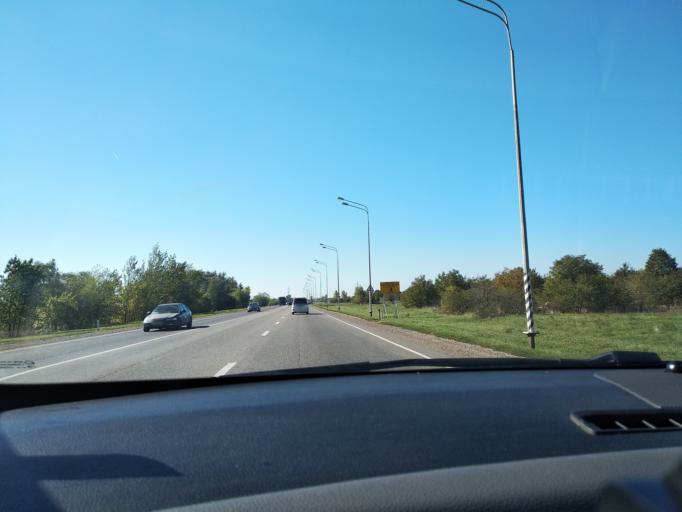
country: RU
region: Krasnodarskiy
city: Agronom
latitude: 45.1658
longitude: 39.0872
